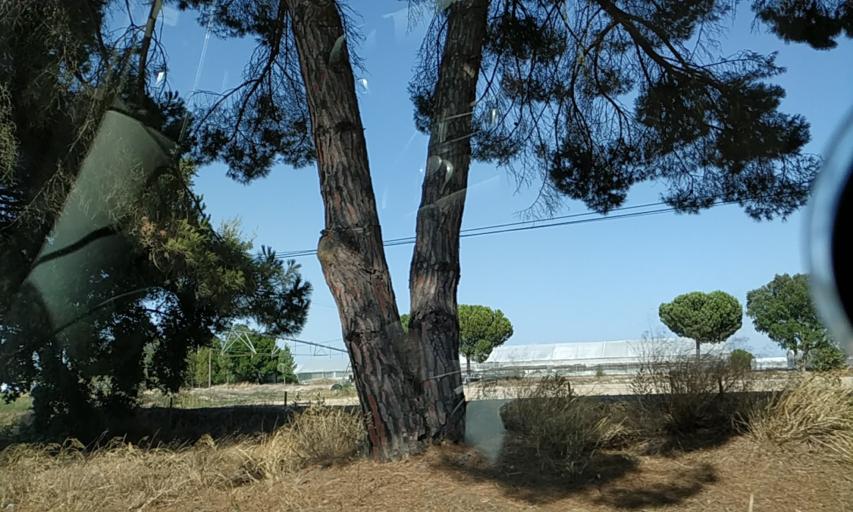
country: PT
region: Evora
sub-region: Vendas Novas
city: Vendas Novas
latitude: 38.7126
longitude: -8.6162
